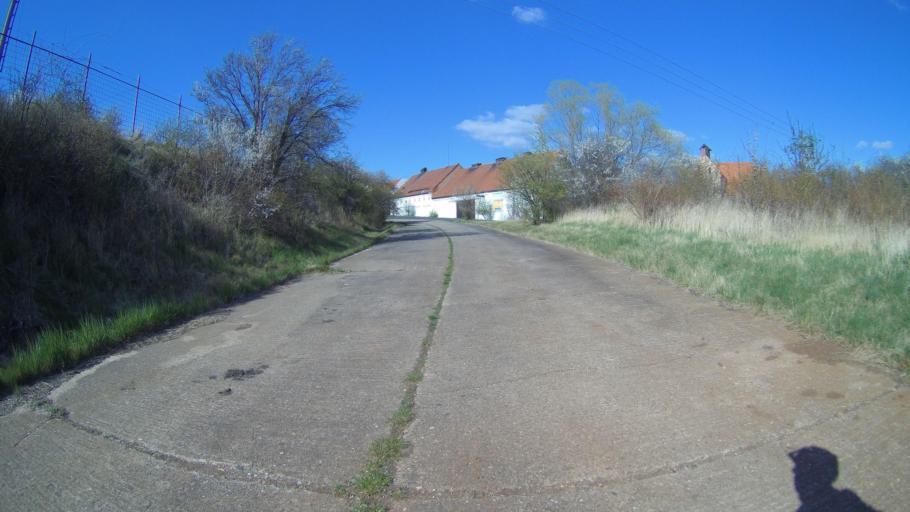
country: CZ
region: Ustecky
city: Brezno
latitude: 50.3600
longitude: 13.4202
